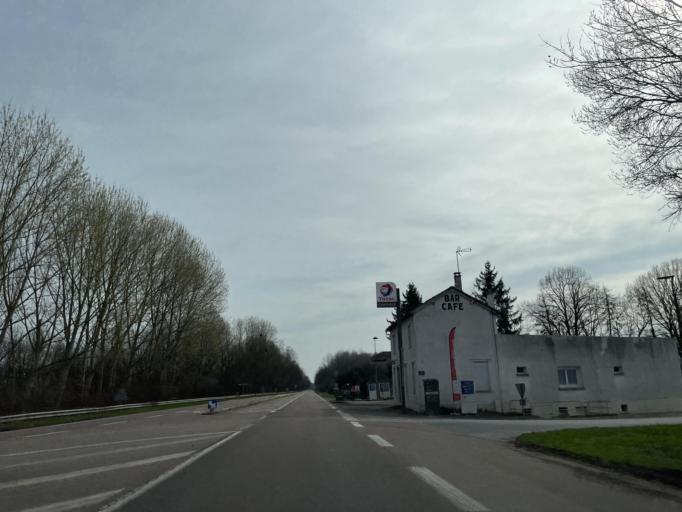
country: FR
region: Champagne-Ardenne
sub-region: Departement de l'Aube
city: Nogent-sur-Seine
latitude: 48.5063
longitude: 3.4389
